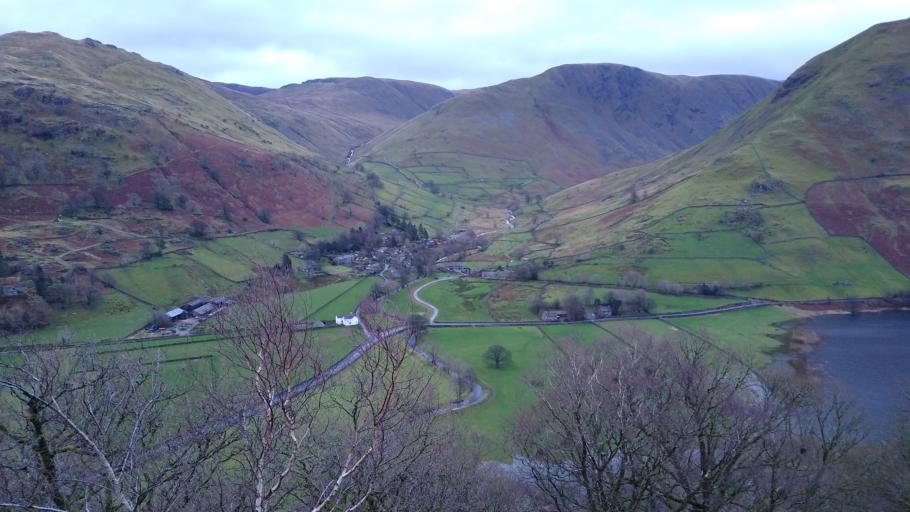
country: GB
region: England
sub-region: Cumbria
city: Ambleside
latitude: 54.5113
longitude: -2.9283
